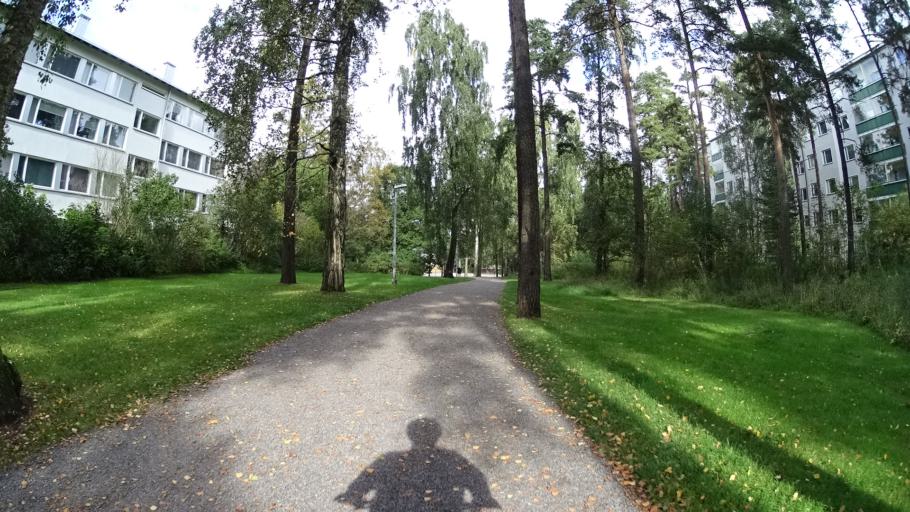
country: FI
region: Uusimaa
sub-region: Helsinki
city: Teekkarikylae
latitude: 60.2045
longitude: 24.8721
